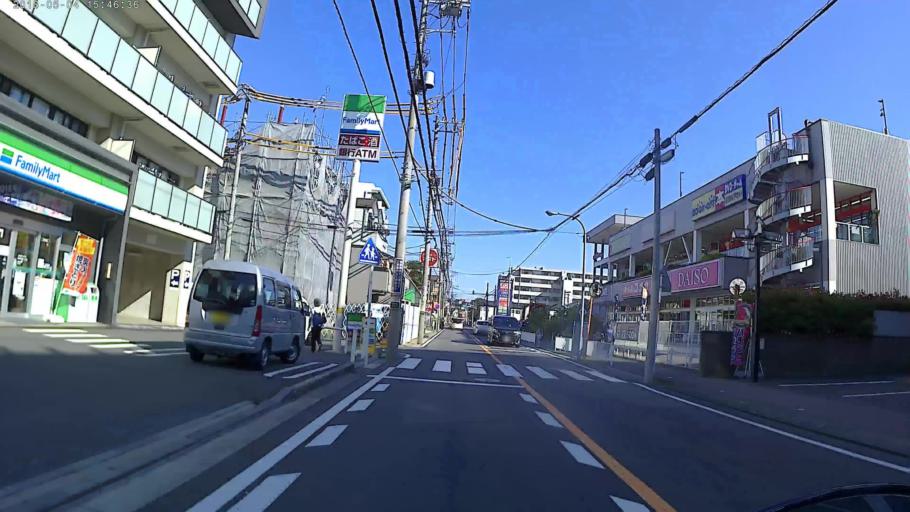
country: JP
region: Kanagawa
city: Yokohama
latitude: 35.5016
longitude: 139.6439
